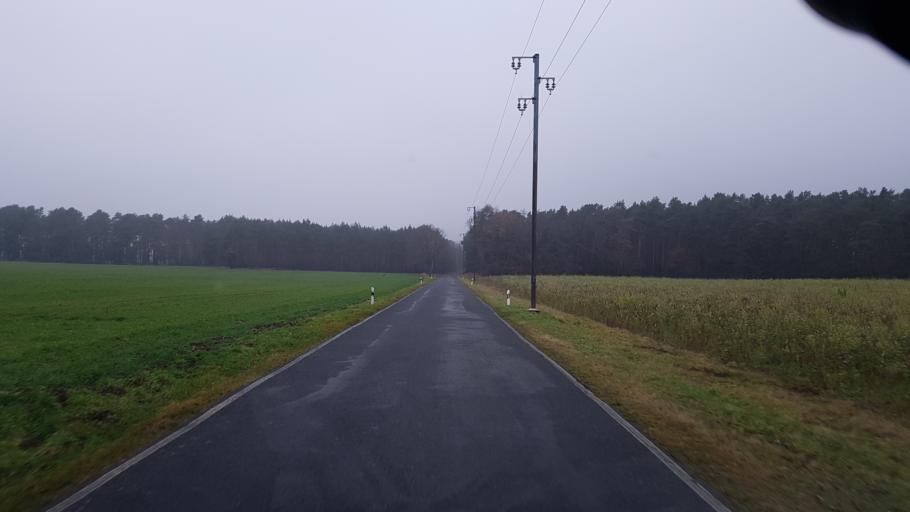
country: DE
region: Brandenburg
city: Altdobern
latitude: 51.6821
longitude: 13.9803
